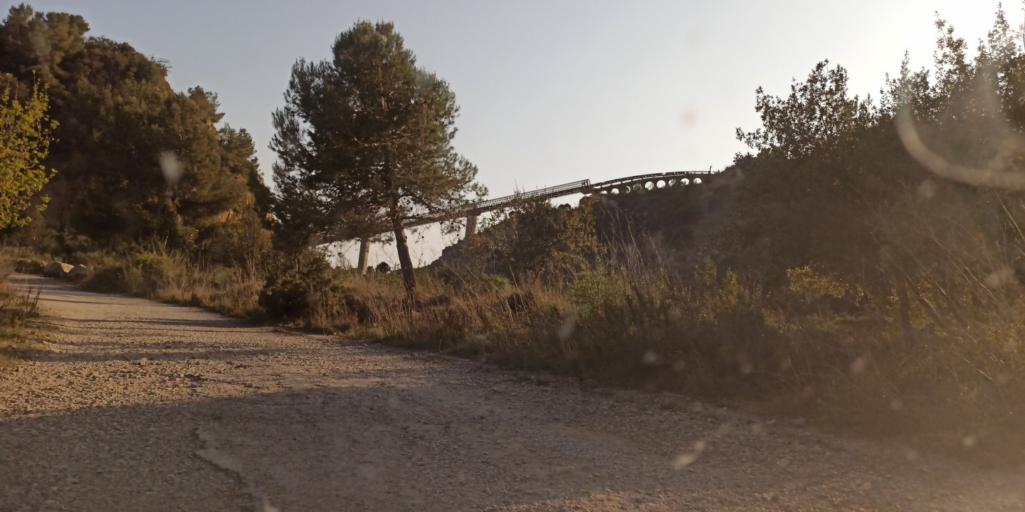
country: ES
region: Catalonia
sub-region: Provincia de Barcelona
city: Sant Feliu de Llobregat
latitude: 41.4119
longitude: 2.0574
